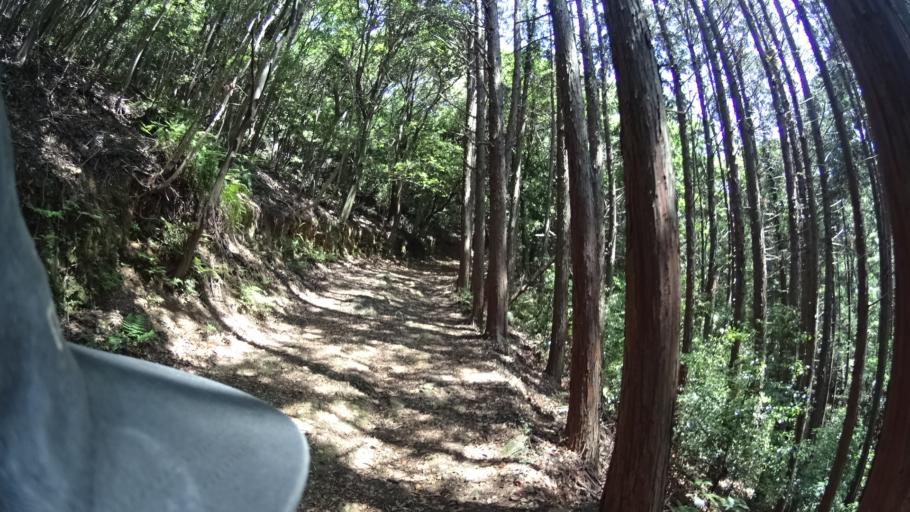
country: JP
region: Shizuoka
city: Kosai-shi
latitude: 34.7390
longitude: 137.4870
